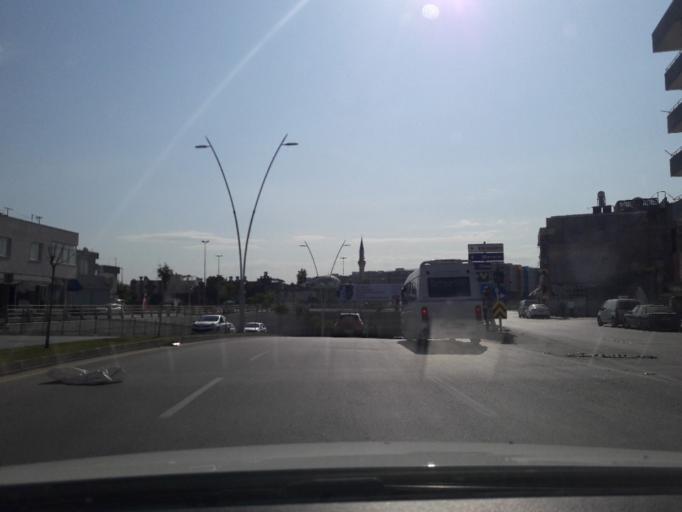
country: TR
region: Adana
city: Seyhan
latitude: 36.9987
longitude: 35.3006
